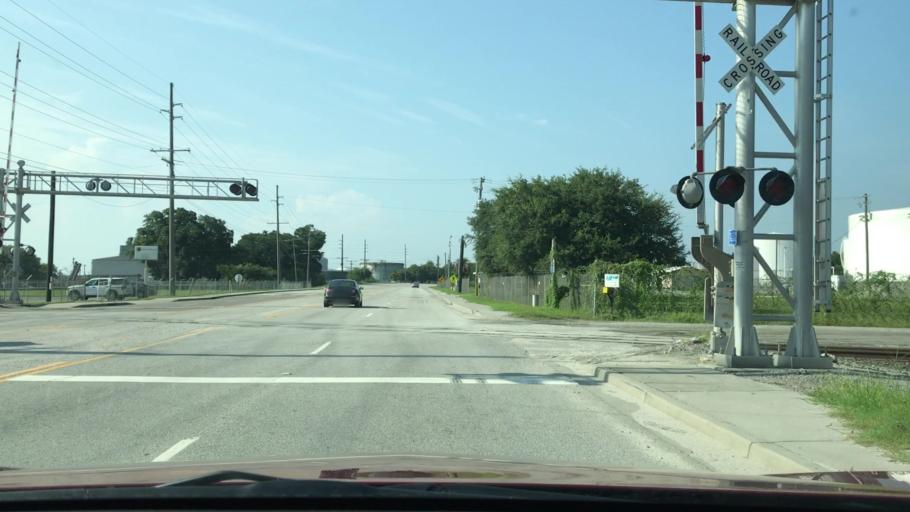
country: US
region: South Carolina
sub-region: Charleston County
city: North Charleston
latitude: 32.8901
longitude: -79.9729
